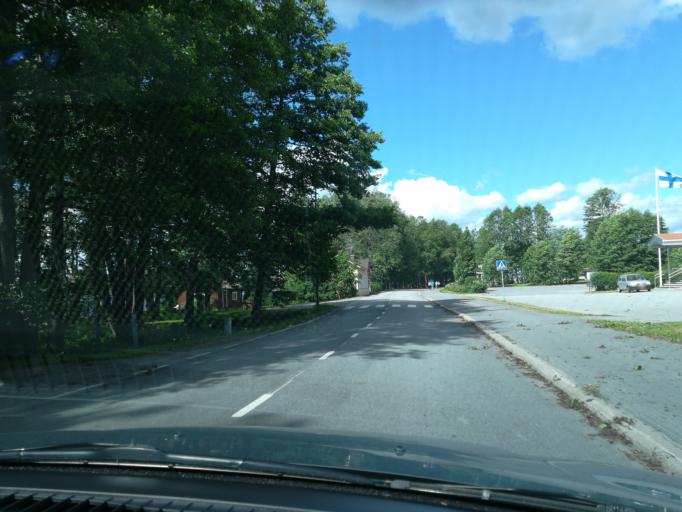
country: FI
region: Southern Savonia
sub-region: Mikkeli
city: Hirvensalmi
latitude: 61.6404
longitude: 26.7751
